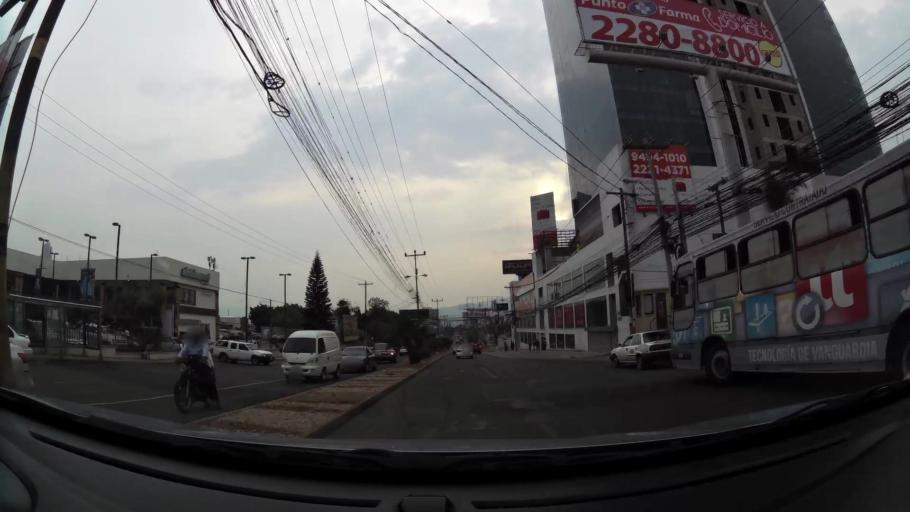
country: HN
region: Francisco Morazan
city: Tegucigalpa
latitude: 14.1004
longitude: -87.1822
